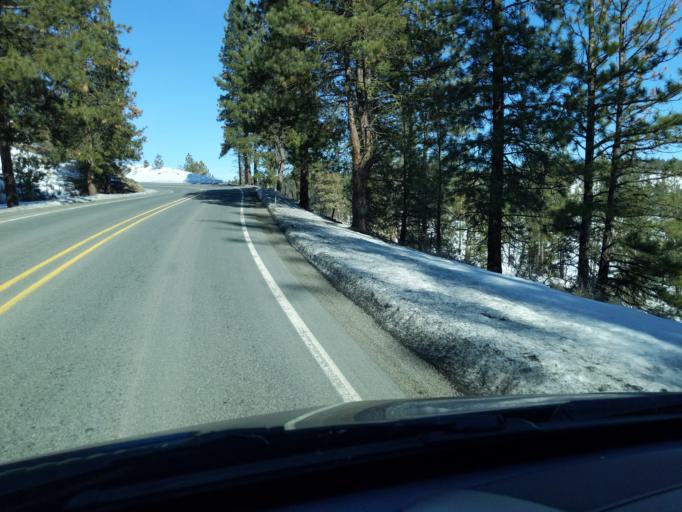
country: US
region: Oregon
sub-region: Grant County
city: John Day
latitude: 44.9075
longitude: -119.0107
